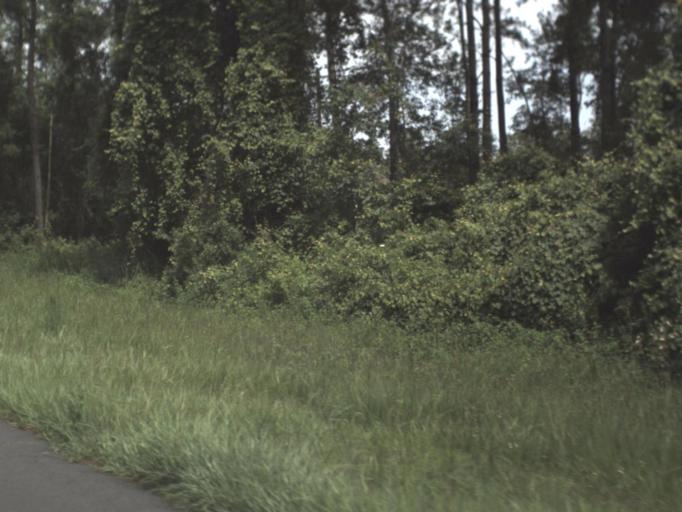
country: US
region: Florida
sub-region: Jefferson County
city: Monticello
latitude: 30.4848
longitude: -83.6981
